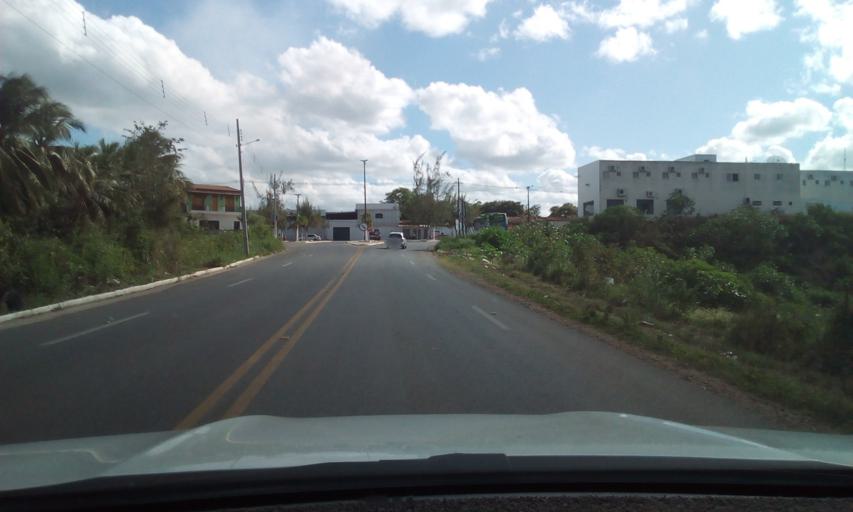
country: BR
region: Paraiba
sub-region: Guarabira
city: Guarabira
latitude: -6.8672
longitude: -35.4884
